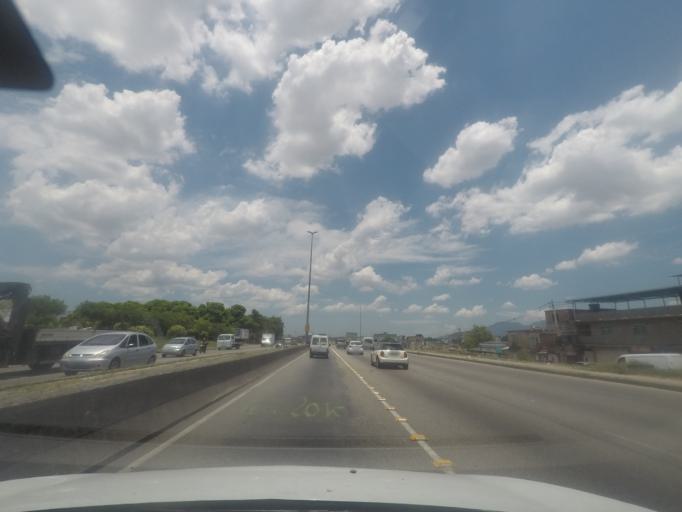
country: BR
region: Rio de Janeiro
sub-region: Sao Joao De Meriti
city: Sao Joao de Meriti
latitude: -22.8281
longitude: -43.3433
